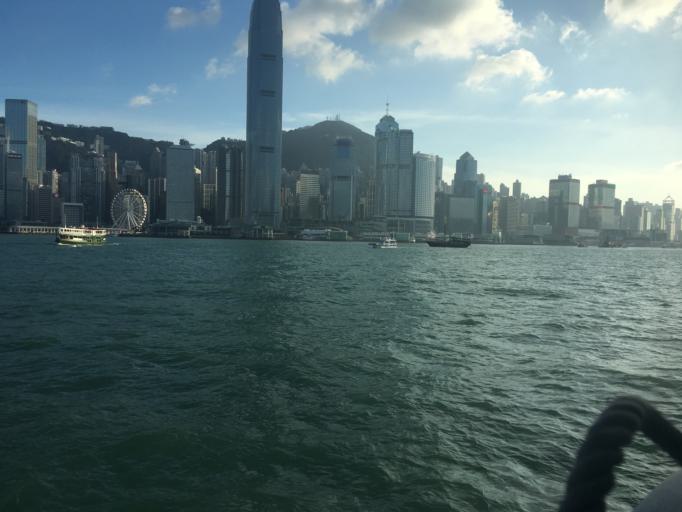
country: HK
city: Hong Kong
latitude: 22.2920
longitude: 114.1660
